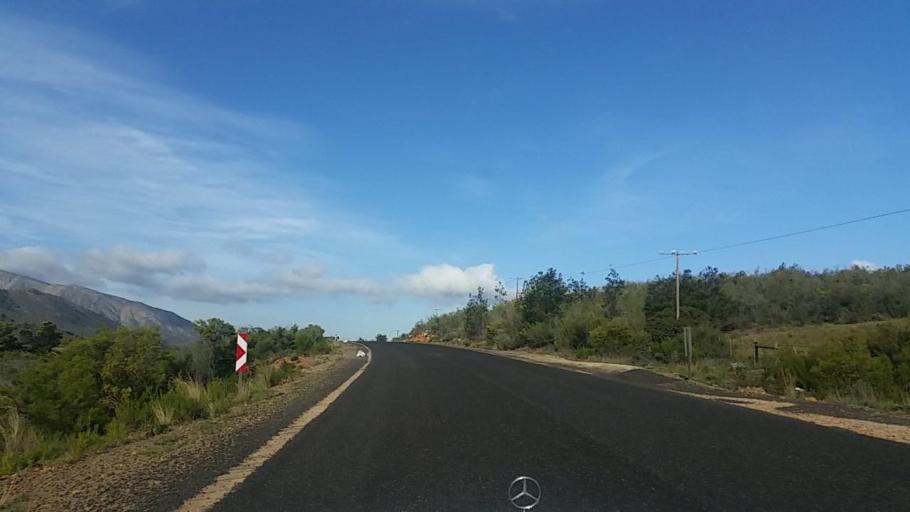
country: ZA
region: Western Cape
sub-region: Eden District Municipality
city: George
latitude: -33.8278
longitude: 22.4017
